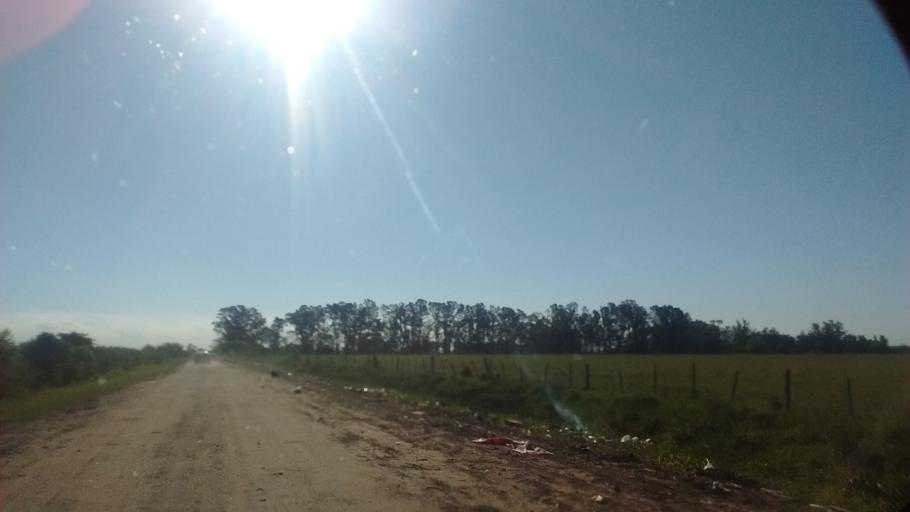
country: AR
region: Santa Fe
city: Funes
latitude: -32.8935
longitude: -60.7999
